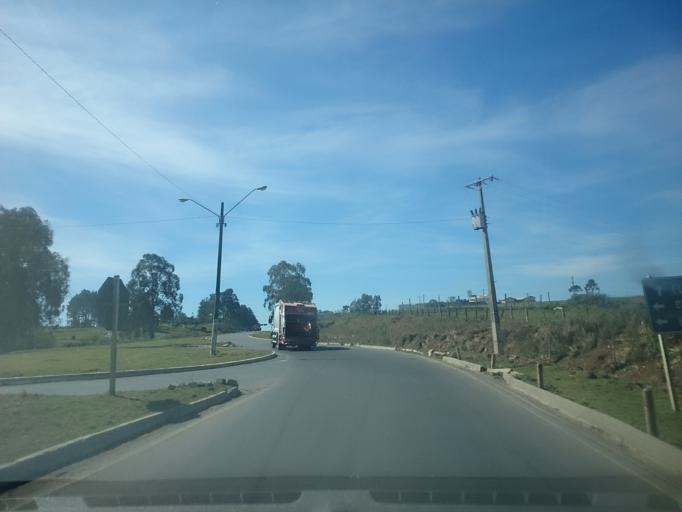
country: BR
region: Santa Catarina
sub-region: Lages
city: Lages
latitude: -27.7738
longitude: -50.2023
